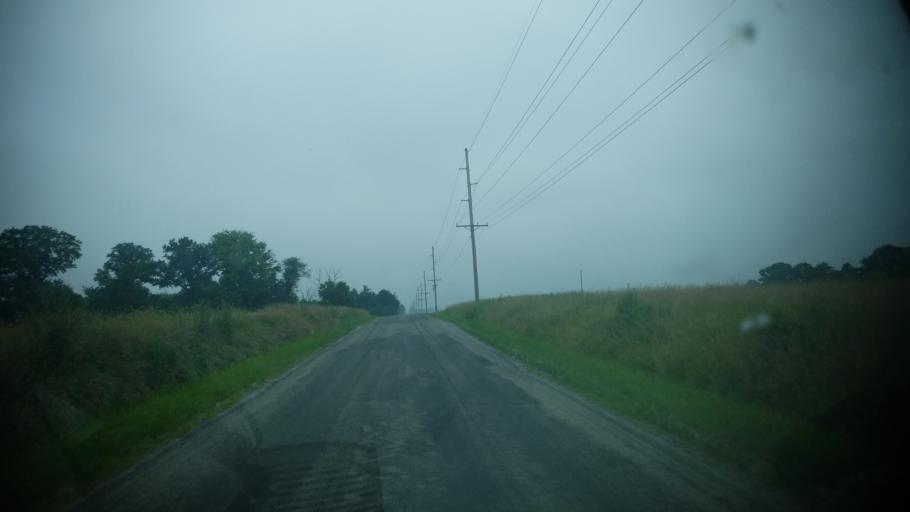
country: US
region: Illinois
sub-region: Wayne County
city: Fairfield
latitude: 38.5286
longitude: -88.4023
